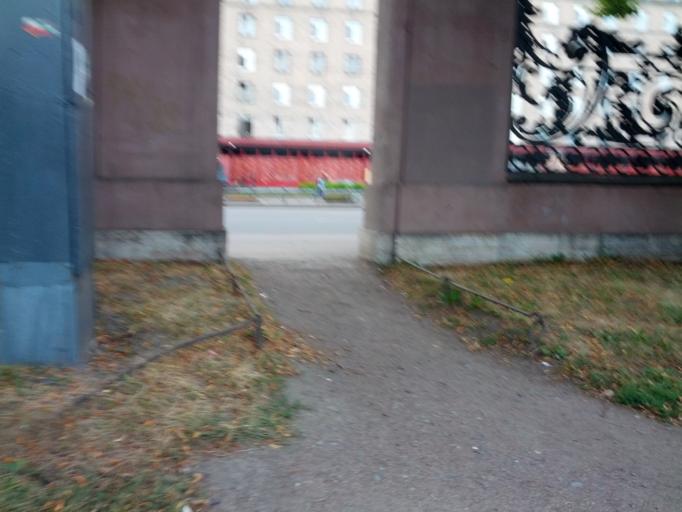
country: RU
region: St.-Petersburg
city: Admiralteisky
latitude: 59.8915
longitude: 30.2732
